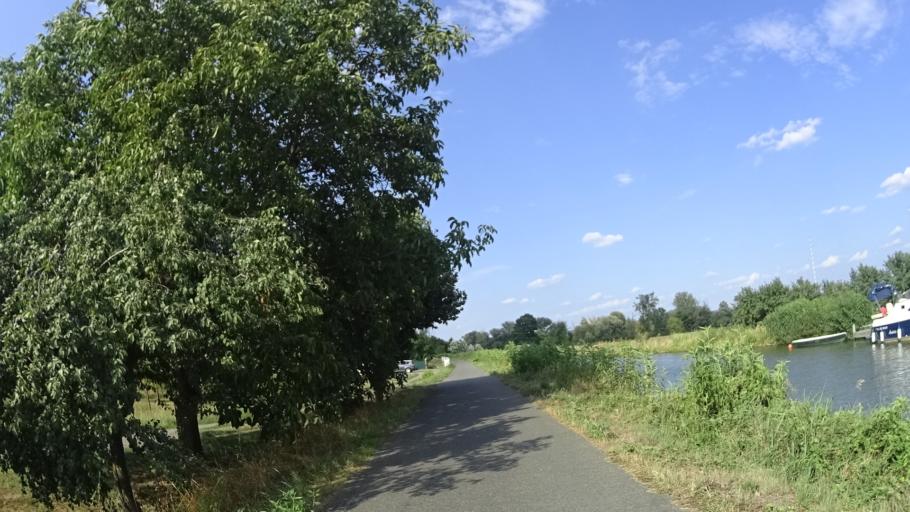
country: CZ
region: Zlin
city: Babice
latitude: 49.1197
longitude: 17.4874
